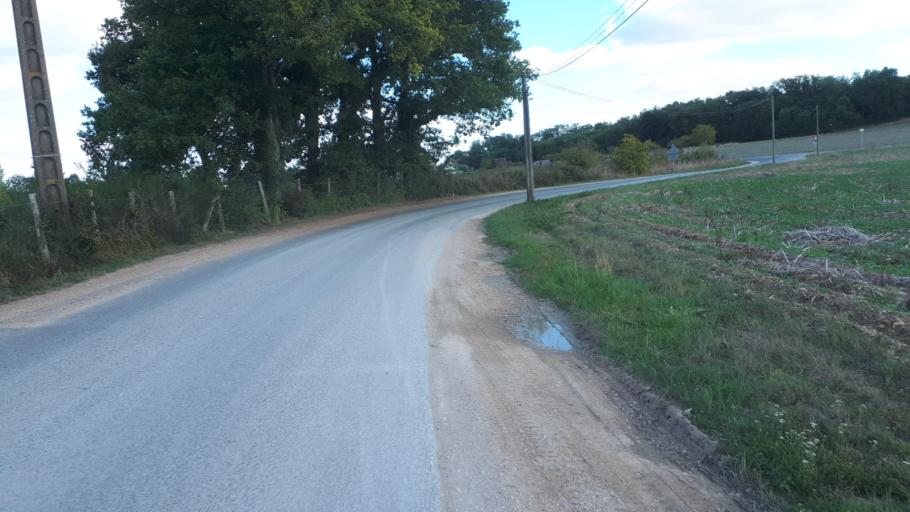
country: FR
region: Centre
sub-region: Departement du Loir-et-Cher
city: Villiers-sur-Loir
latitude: 47.8068
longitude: 0.9713
